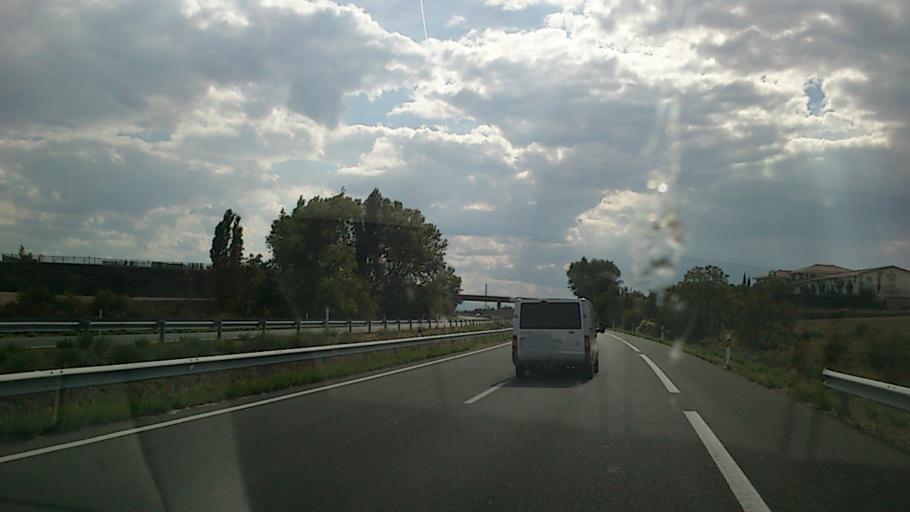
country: ES
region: La Rioja
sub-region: Provincia de La Rioja
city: Anguciana
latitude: 42.5756
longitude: -2.8780
